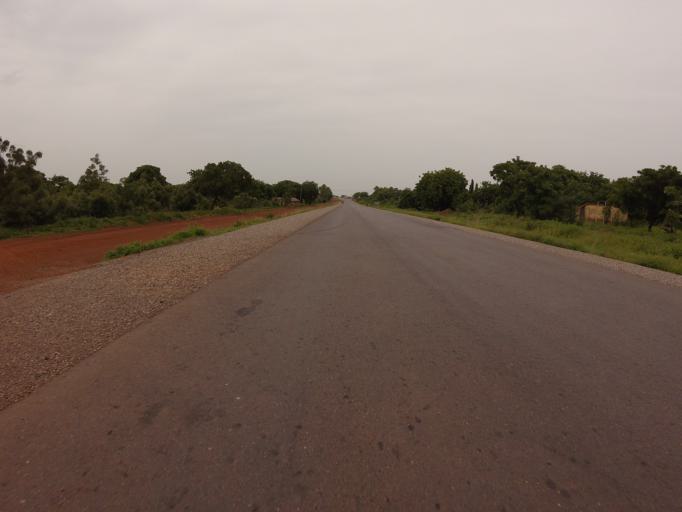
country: GH
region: Northern
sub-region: Yendi
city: Yendi
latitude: 9.3082
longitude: 0.0167
